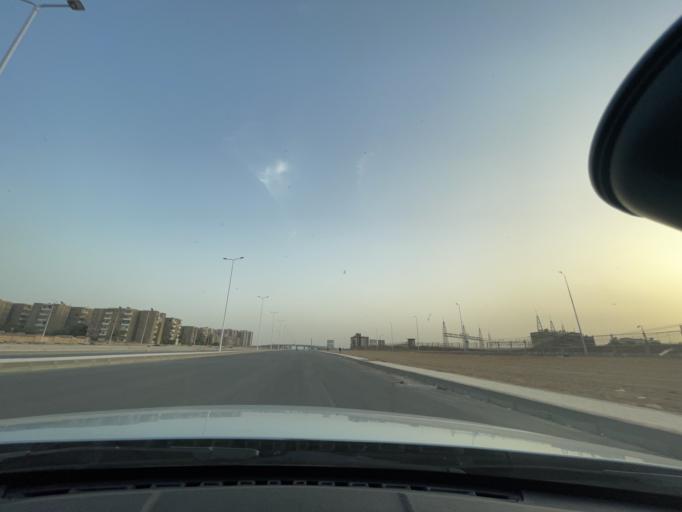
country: EG
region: Muhafazat al Qahirah
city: Cairo
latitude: 30.0407
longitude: 31.3593
